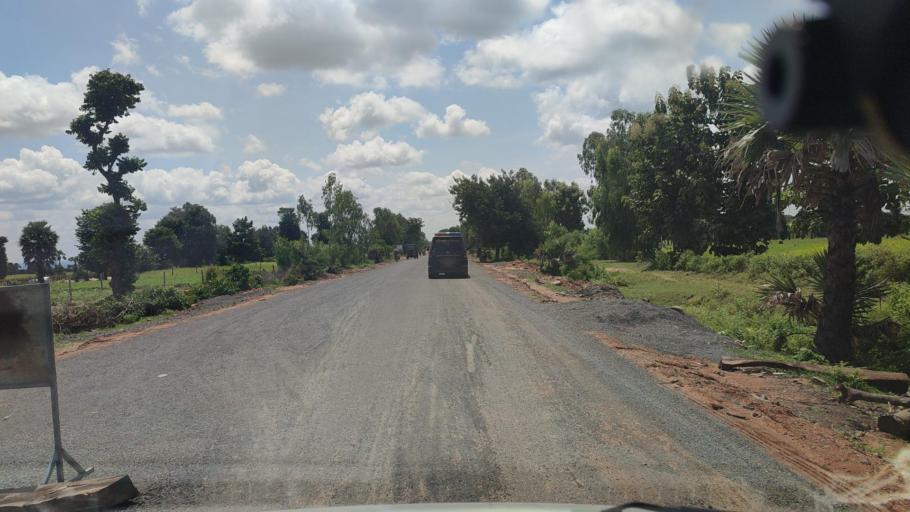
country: MM
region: Magway
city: Magway
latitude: 20.1945
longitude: 95.0802
